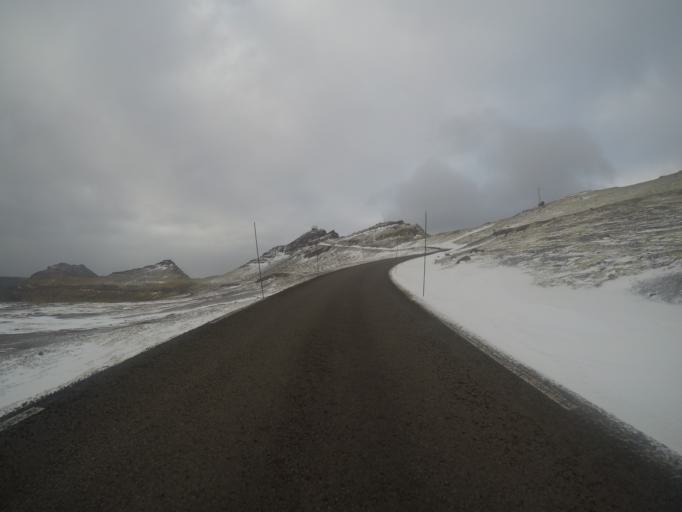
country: FO
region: Streymoy
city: Kollafjordhur
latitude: 62.0768
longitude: -6.9582
